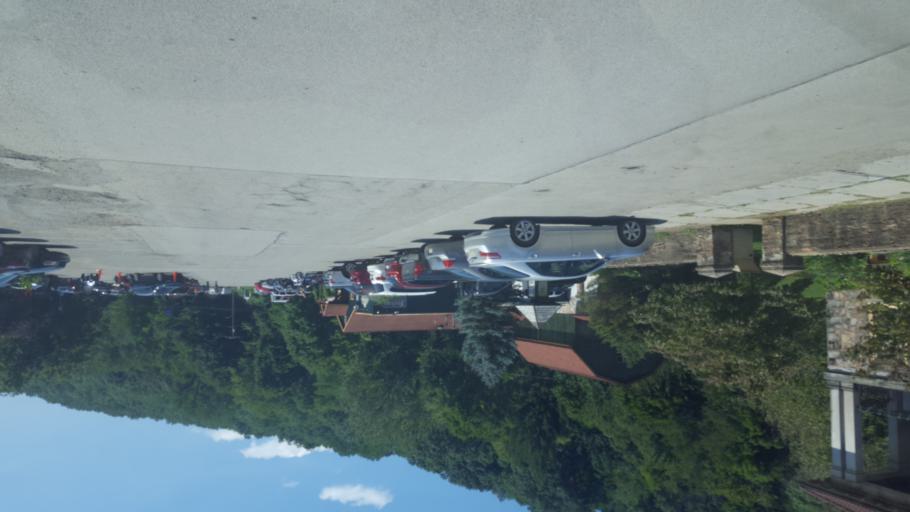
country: US
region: Pennsylvania
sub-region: Clarion County
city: Knox
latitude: 41.1404
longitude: -79.6793
